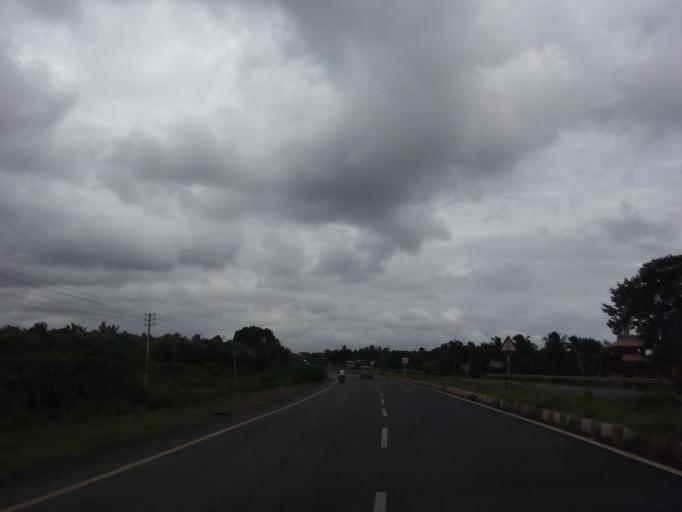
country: IN
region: Karnataka
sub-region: Haveri
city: Ranibennur
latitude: 14.6339
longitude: 75.5840
